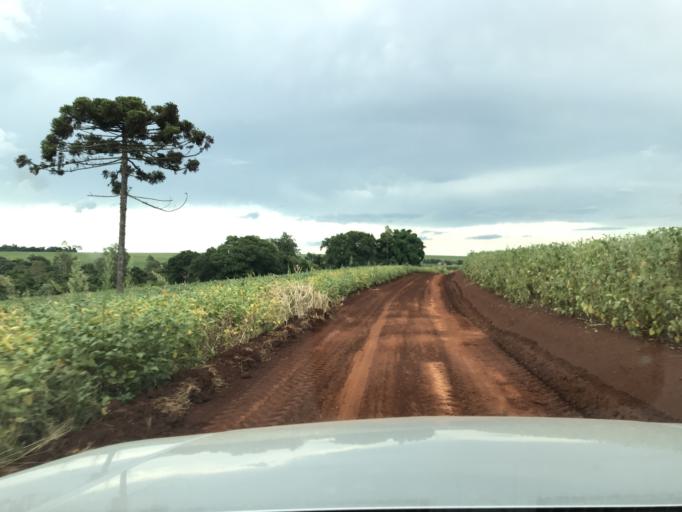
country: BR
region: Parana
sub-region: Palotina
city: Palotina
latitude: -24.2690
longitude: -53.7713
